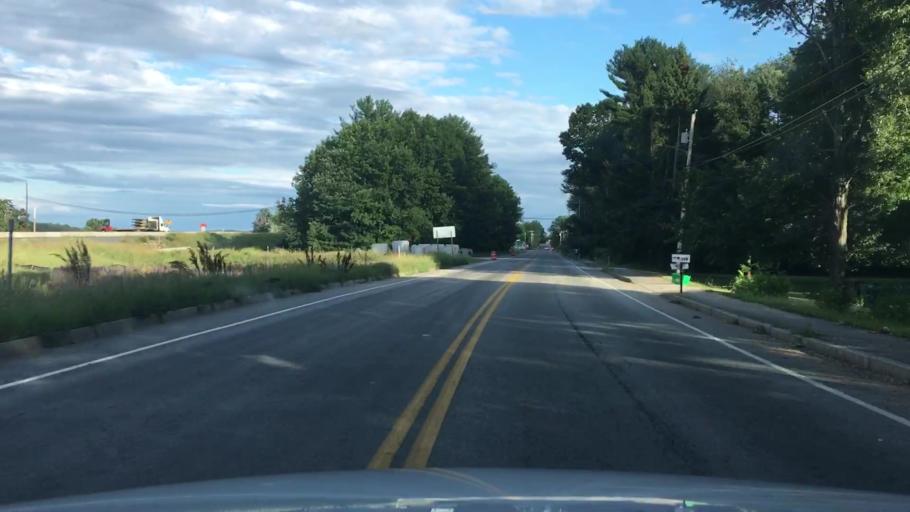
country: US
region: Maine
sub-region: York County
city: Eliot
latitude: 43.1270
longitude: -70.8399
